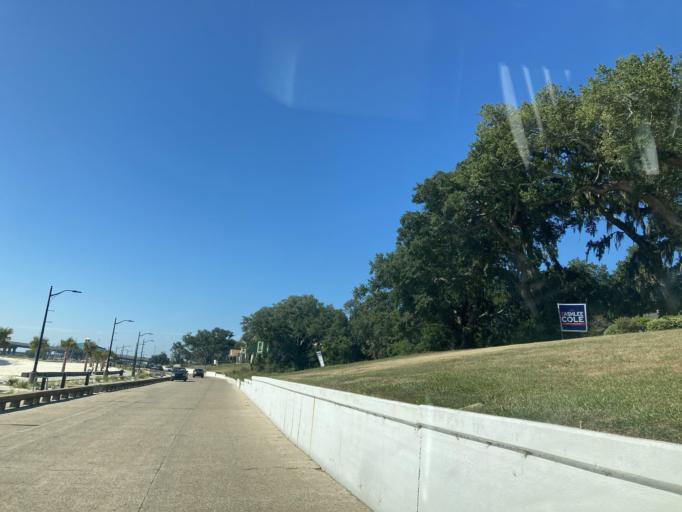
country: US
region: Mississippi
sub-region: Jackson County
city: Ocean Springs
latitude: 30.4087
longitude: -88.8370
